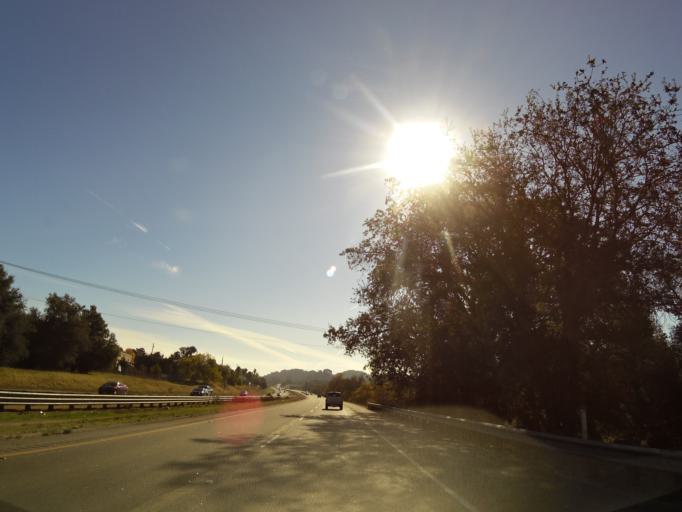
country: US
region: California
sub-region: San Luis Obispo County
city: Atascadero
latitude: 35.5049
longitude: -120.6933
